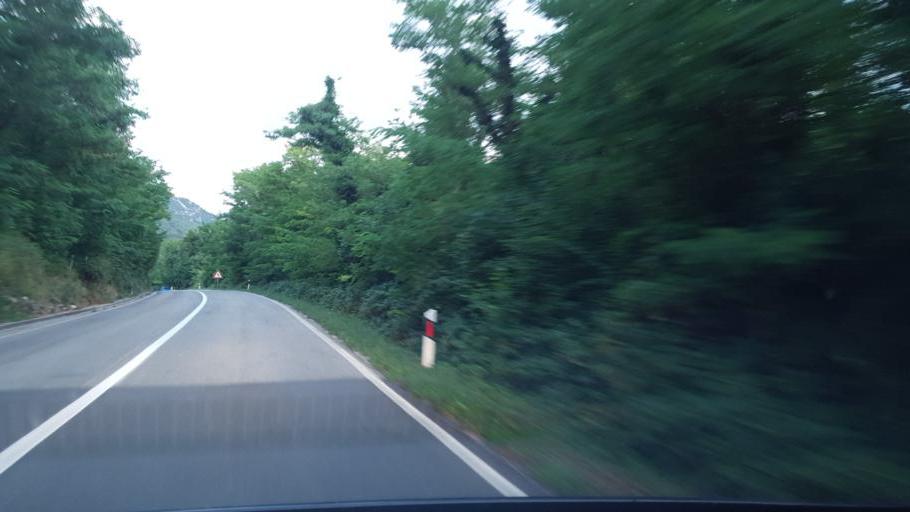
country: HR
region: Primorsko-Goranska
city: Punat
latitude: 45.0164
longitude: 14.6941
